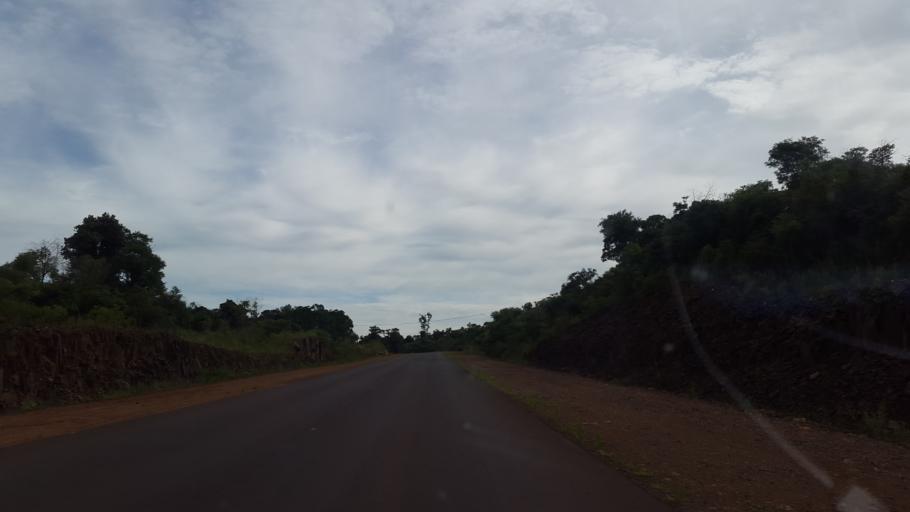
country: AR
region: Misiones
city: Bernardo de Irigoyen
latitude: -26.4428
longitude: -53.8576
